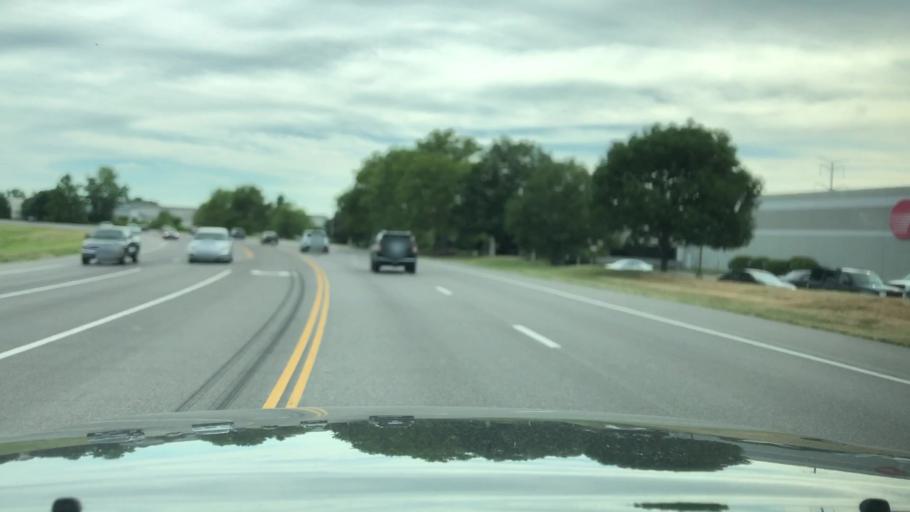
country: US
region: Missouri
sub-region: Saint Charles County
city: Saint Charles
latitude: 38.7875
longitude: -90.4582
